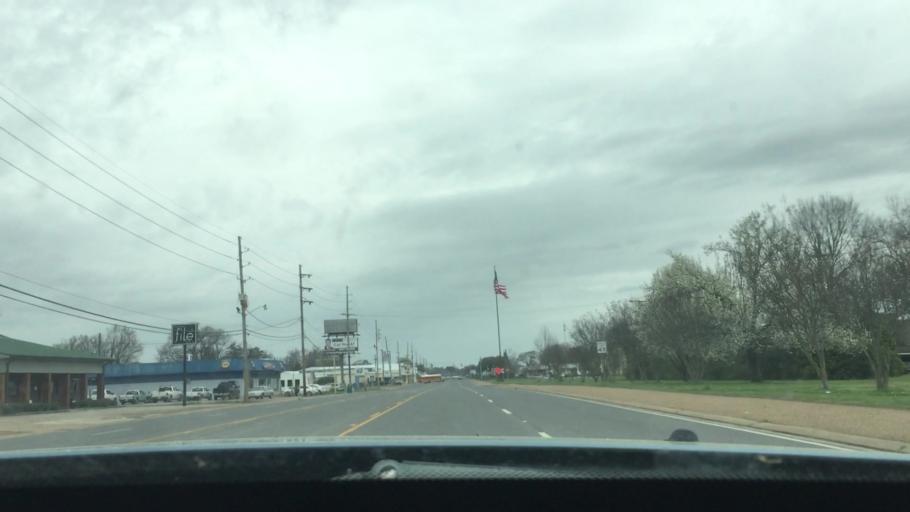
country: US
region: Louisiana
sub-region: Franklin Parish
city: Winnsboro
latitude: 32.1611
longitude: -91.7183
